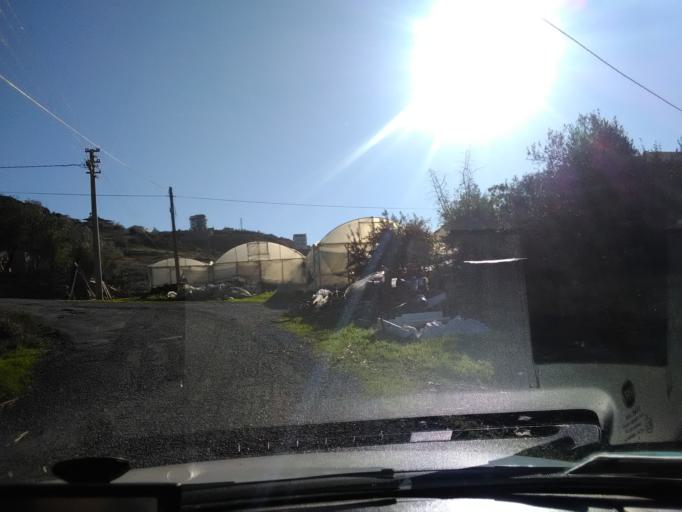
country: TR
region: Antalya
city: Gazipasa
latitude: 36.2438
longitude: 32.3033
